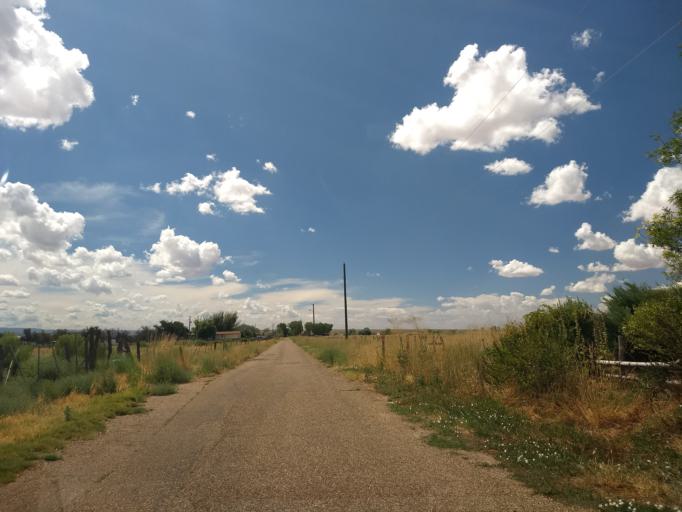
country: US
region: Arizona
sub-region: Coconino County
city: Fredonia
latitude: 36.9446
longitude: -112.5308
